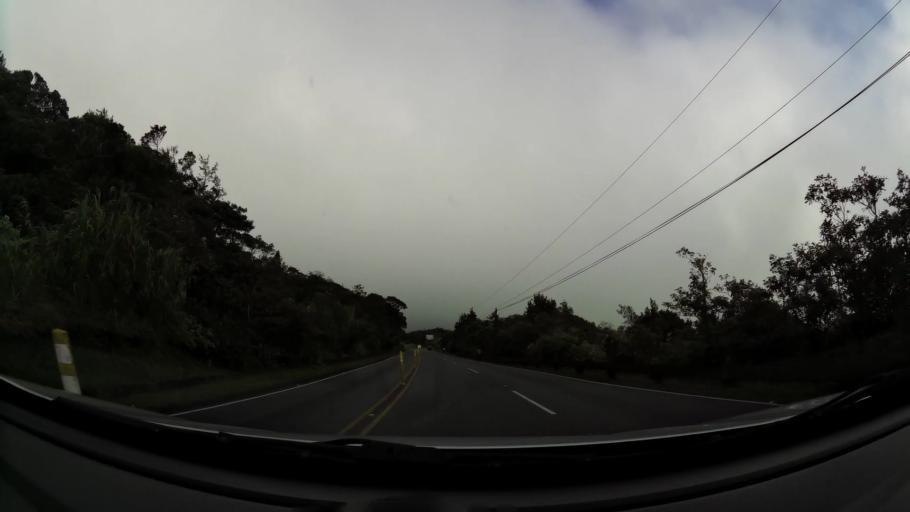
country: CR
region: Heredia
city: Angeles
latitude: 10.0334
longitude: -84.0028
